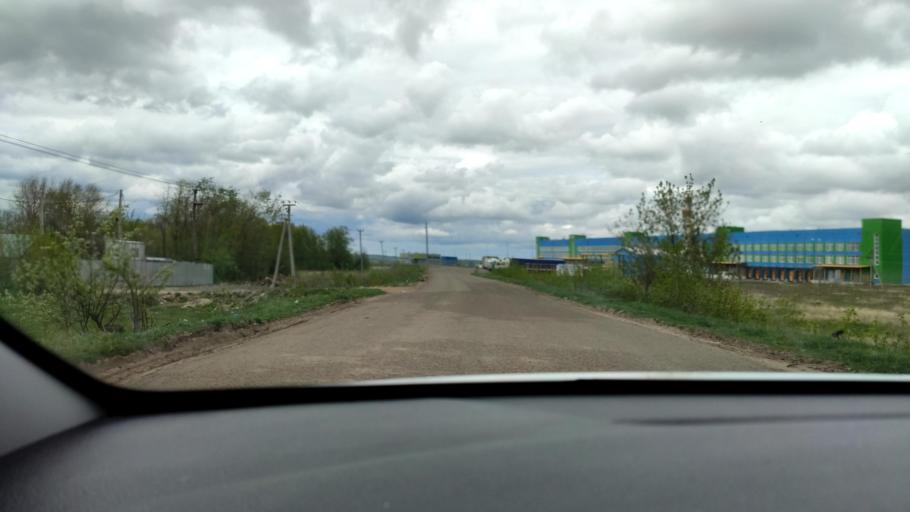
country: RU
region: Tatarstan
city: Vysokaya Gora
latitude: 55.8024
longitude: 49.3129
